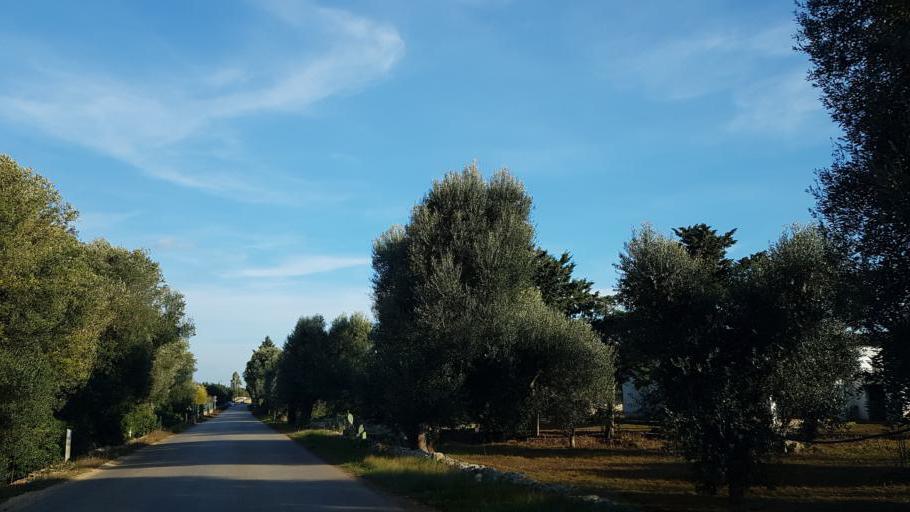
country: IT
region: Apulia
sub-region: Provincia di Brindisi
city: San Vito dei Normanni
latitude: 40.7050
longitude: 17.7110
